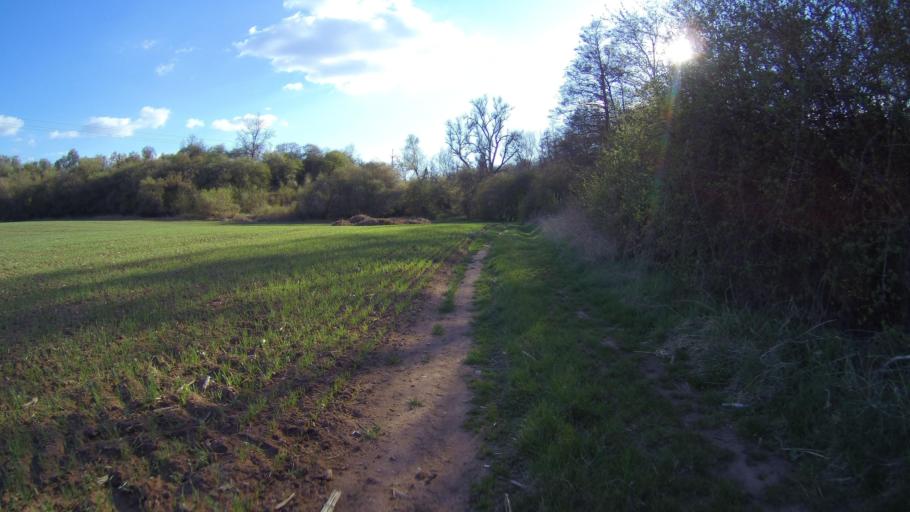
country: CZ
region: Ustecky
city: Zatec
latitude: 50.3121
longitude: 13.5994
